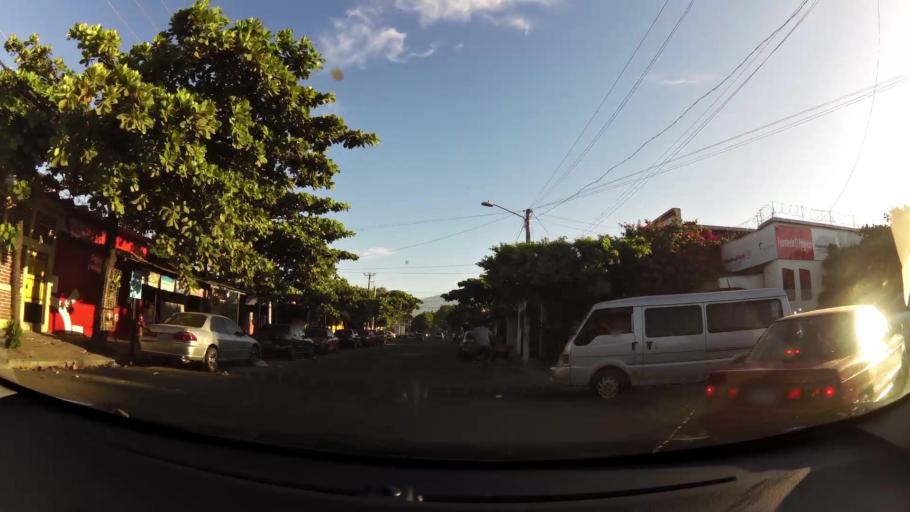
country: SV
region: Sonsonate
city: Sonsonate
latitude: 13.7132
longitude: -89.7289
